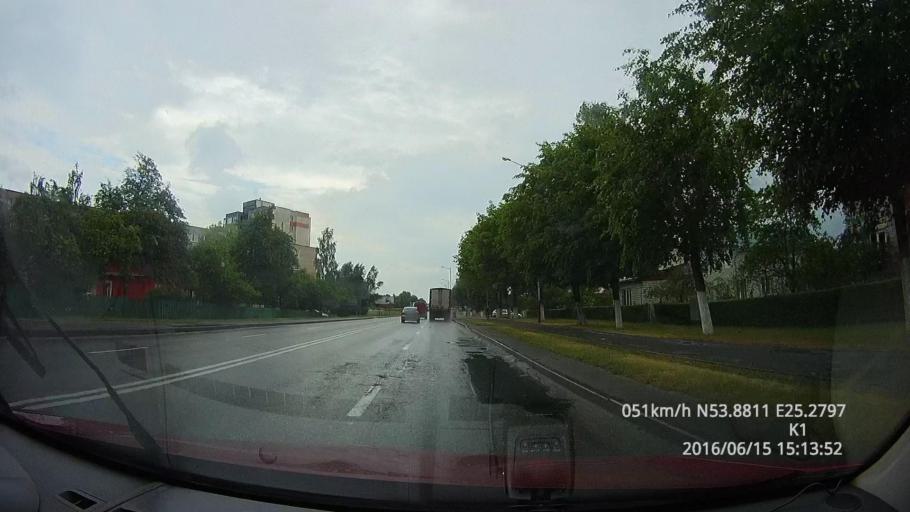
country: BY
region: Grodnenskaya
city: Lida
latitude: 53.8809
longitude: 25.2794
